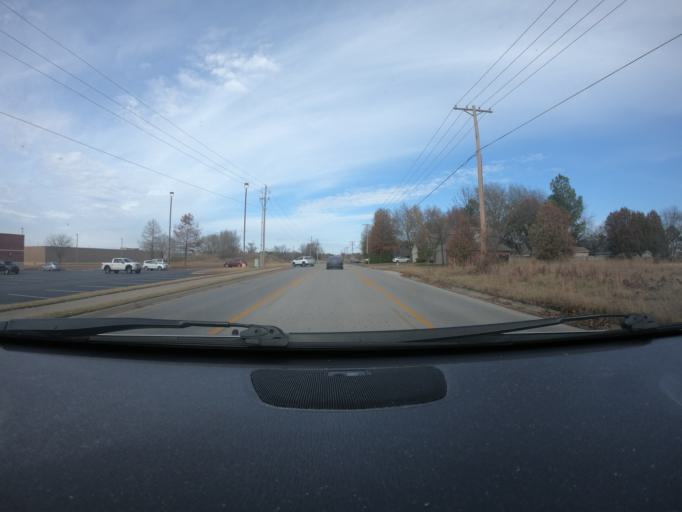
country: US
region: Arkansas
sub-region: Benton County
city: Bentonville
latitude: 36.3361
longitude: -94.1749
